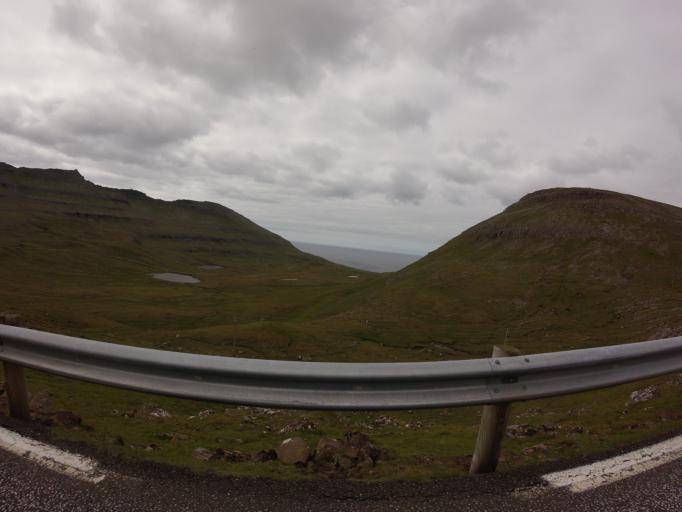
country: FO
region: Suduroy
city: Tvoroyri
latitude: 61.5227
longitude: -6.8372
